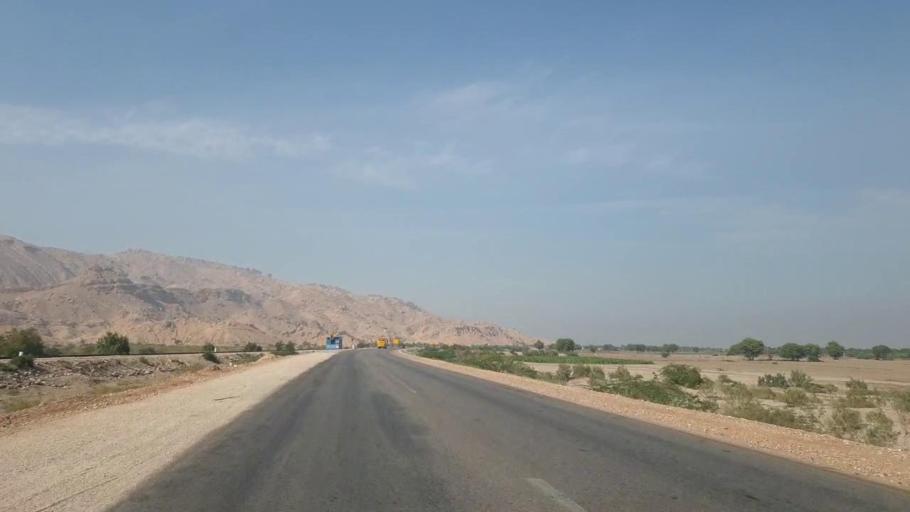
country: PK
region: Sindh
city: Sehwan
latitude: 26.2794
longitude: 67.8969
